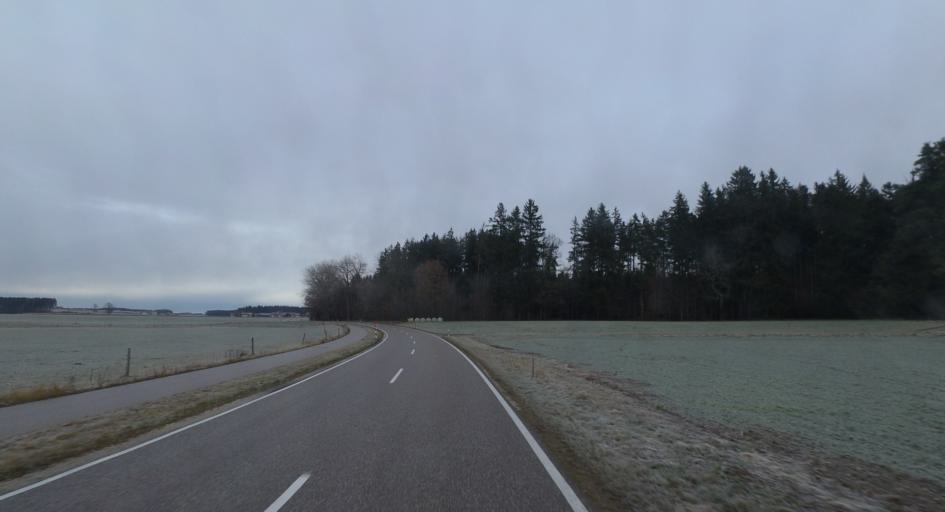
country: DE
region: Bavaria
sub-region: Upper Bavaria
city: Nussdorf
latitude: 47.9331
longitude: 12.6488
